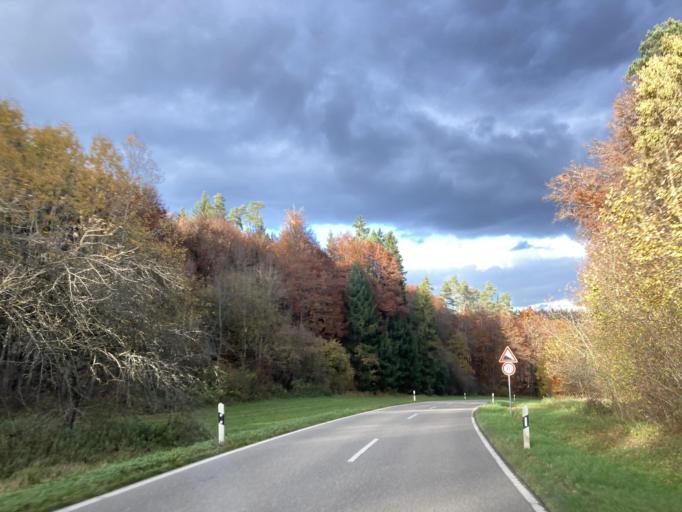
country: DE
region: Baden-Wuerttemberg
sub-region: Karlsruhe Region
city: Empfingen
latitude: 48.4140
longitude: 8.7482
